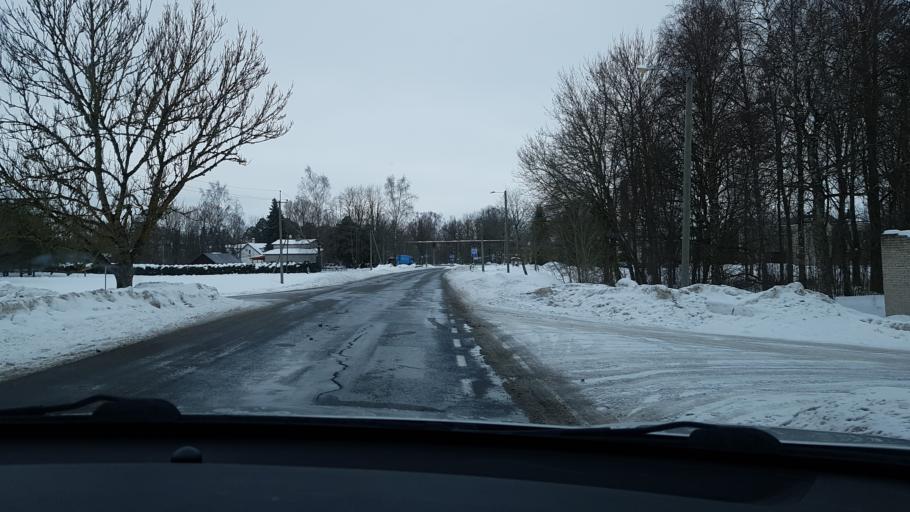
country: EE
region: Jaervamaa
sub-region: Jaerva-Jaani vald
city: Jarva-Jaani
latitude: 59.1459
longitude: 25.7527
